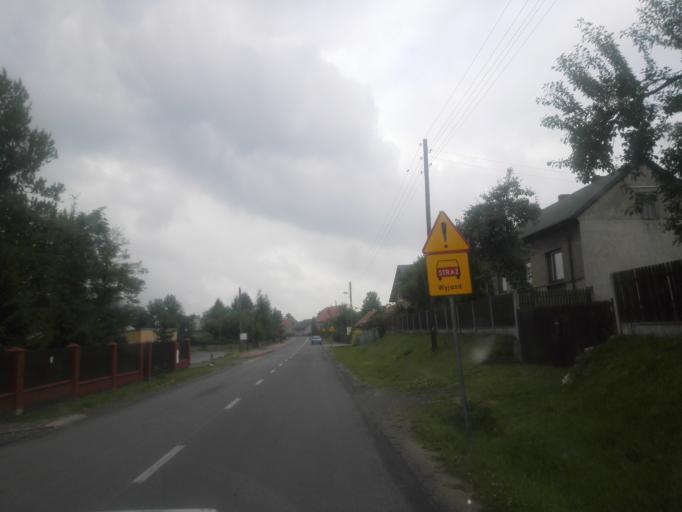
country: PL
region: Silesian Voivodeship
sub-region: Powiat czestochowski
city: Olsztyn
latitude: 50.7264
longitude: 19.3312
